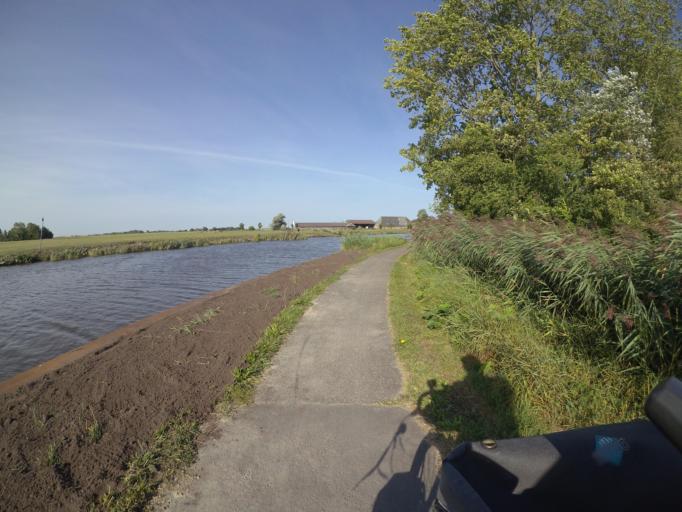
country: NL
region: Friesland
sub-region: Gemeente Dongeradeel
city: Dokkum
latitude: 53.3210
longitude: 5.9732
